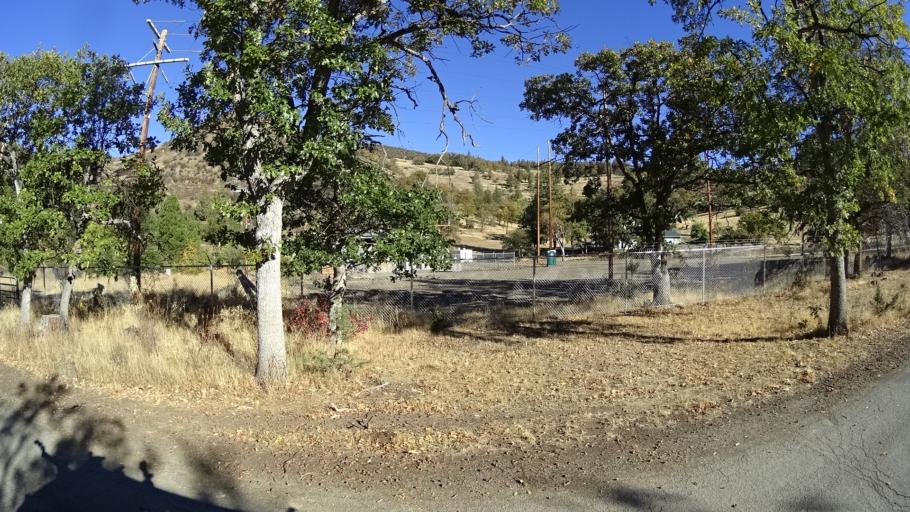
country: US
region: California
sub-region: Siskiyou County
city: Montague
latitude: 41.9849
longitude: -122.3603
